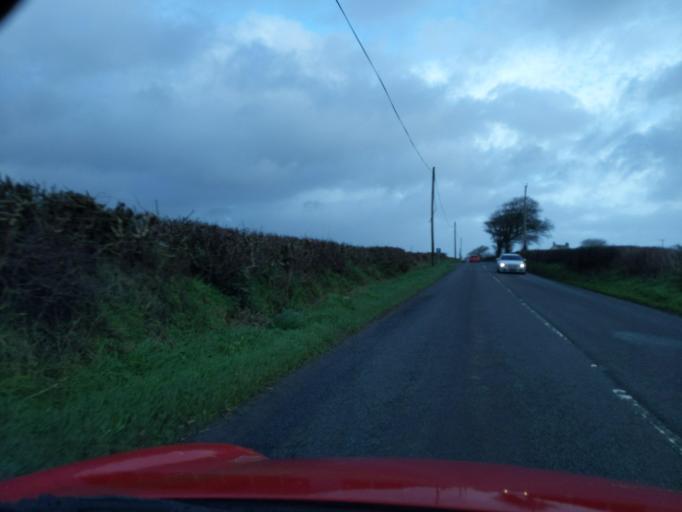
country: GB
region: England
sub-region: Devon
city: Great Torrington
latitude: 50.9014
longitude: -4.2572
